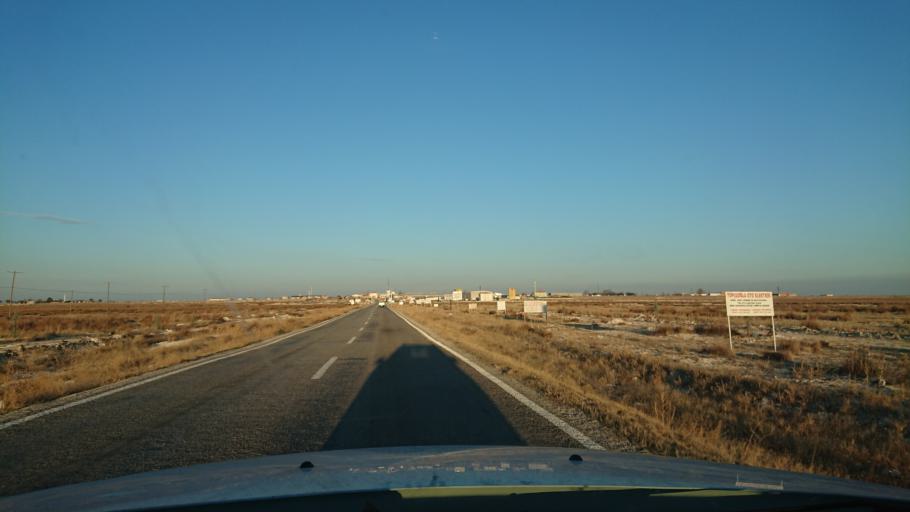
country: TR
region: Aksaray
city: Eskil
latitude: 38.3898
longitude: 33.3869
